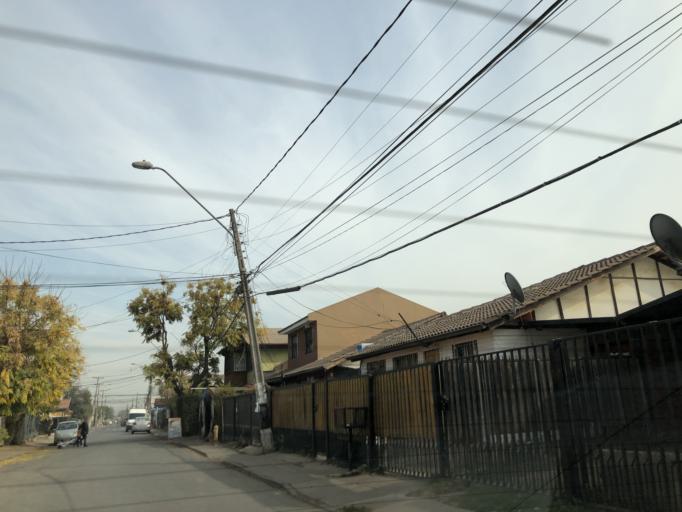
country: CL
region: Santiago Metropolitan
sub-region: Provincia de Cordillera
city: Puente Alto
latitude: -33.5730
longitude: -70.5703
